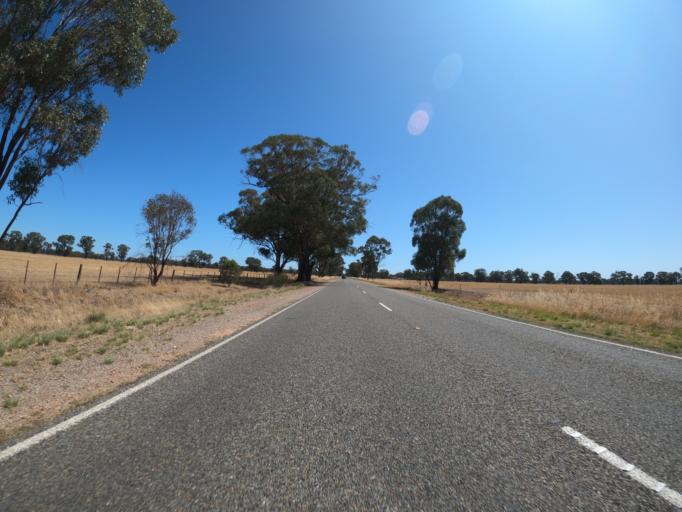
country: AU
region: New South Wales
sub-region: Corowa Shire
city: Corowa
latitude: -36.0738
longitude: 146.3504
